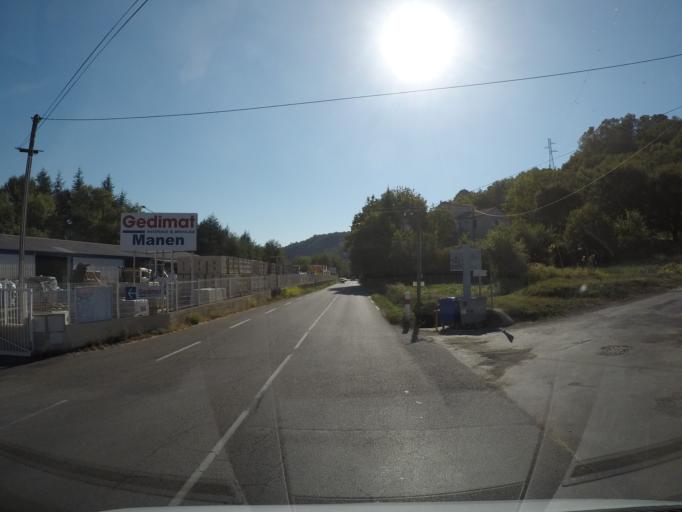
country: FR
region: Languedoc-Roussillon
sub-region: Departement du Gard
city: Anduze
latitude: 44.0405
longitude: 3.9863
